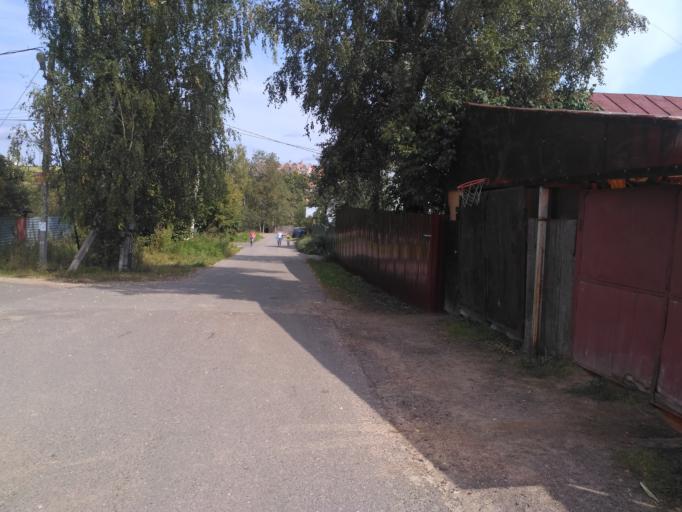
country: RU
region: Moskovskaya
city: Sergiyev Posad
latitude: 56.3180
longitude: 38.1241
